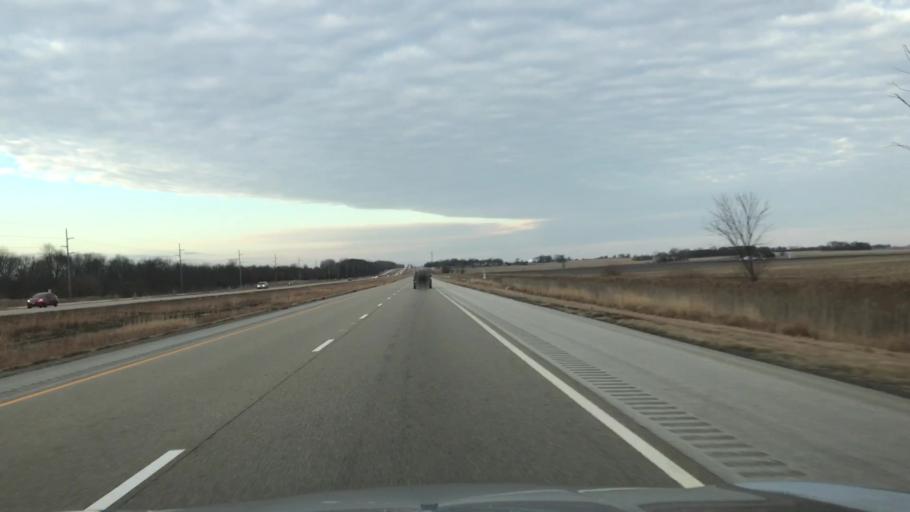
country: US
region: Illinois
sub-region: Logan County
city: Atlanta
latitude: 40.2238
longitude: -89.2739
